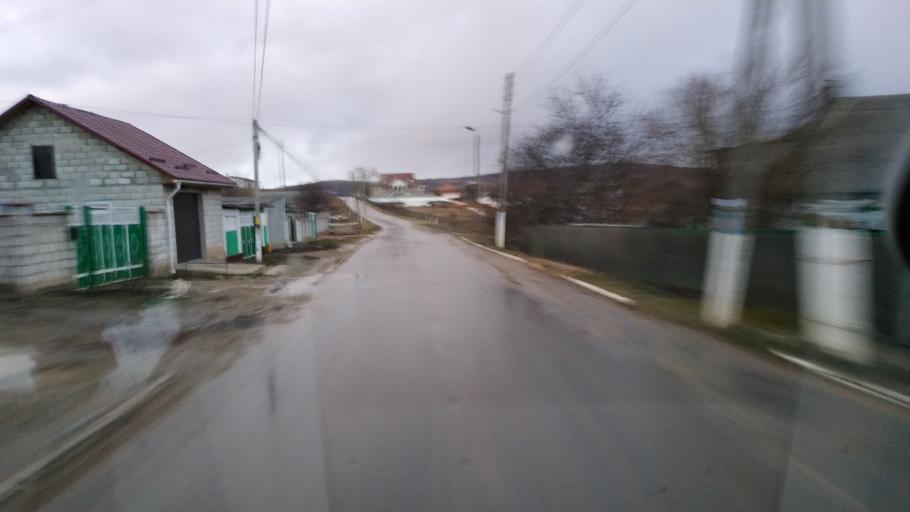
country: MD
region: Taraclia
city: Telenesti
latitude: 47.3840
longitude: 28.3244
